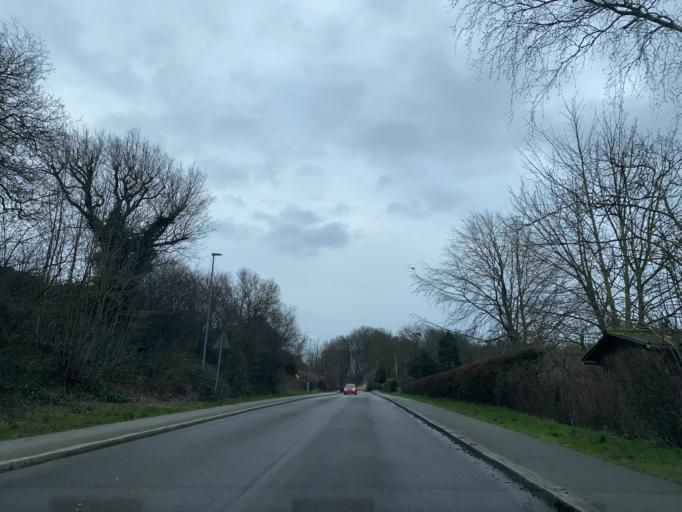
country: DK
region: Central Jutland
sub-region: Viborg Kommune
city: Bjerringbro
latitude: 56.3046
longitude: 9.5953
